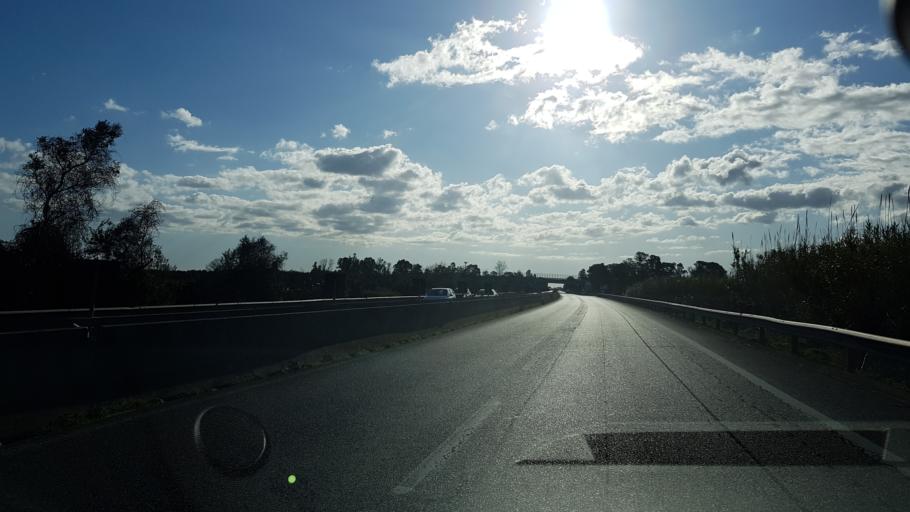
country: IT
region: Apulia
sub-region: Provincia di Brindisi
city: San Pietro Vernotico
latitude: 40.5243
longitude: 18.0143
